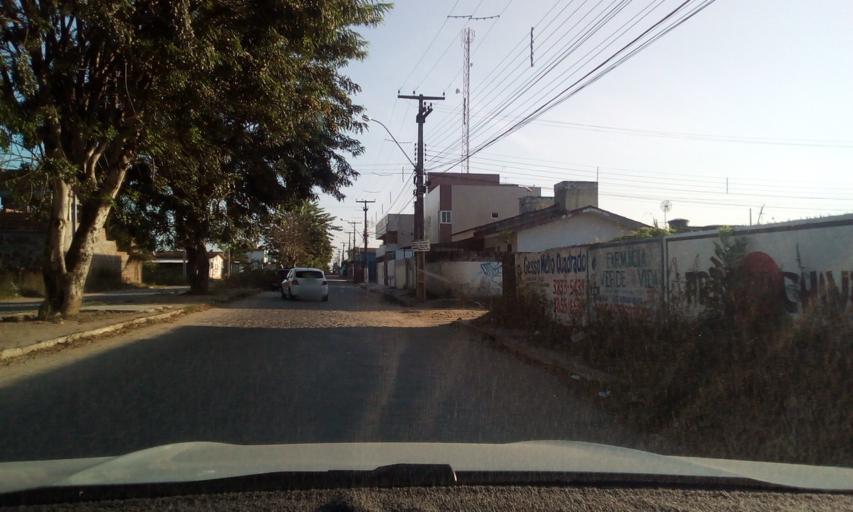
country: BR
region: Paraiba
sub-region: Bayeux
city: Bayeux
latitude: -7.1786
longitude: -34.9329
